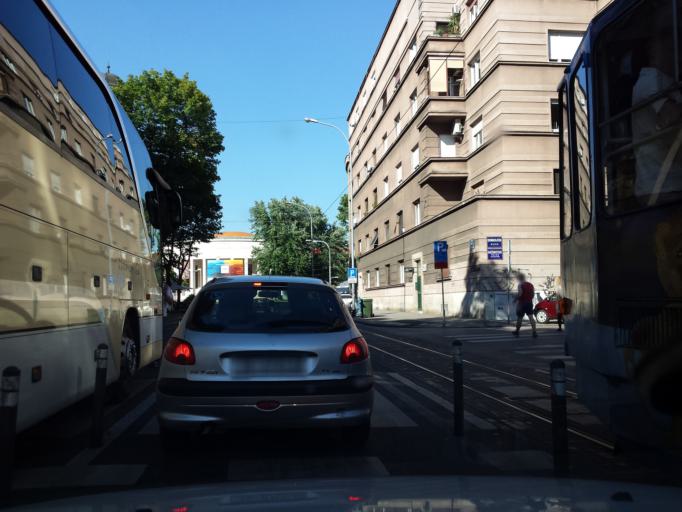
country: HR
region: Grad Zagreb
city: Zagreb - Centar
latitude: 45.8089
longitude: 15.9857
